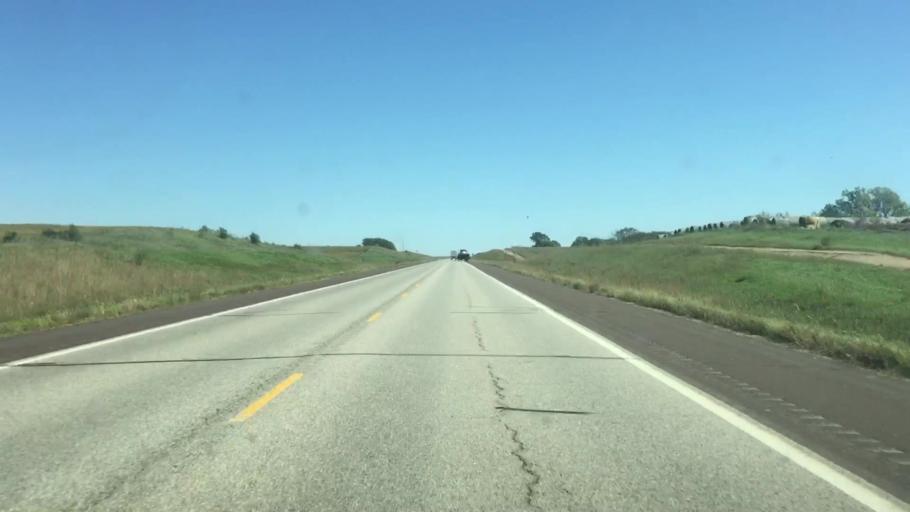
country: US
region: Kansas
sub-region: Nemaha County
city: Seneca
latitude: 39.8421
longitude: -96.2861
